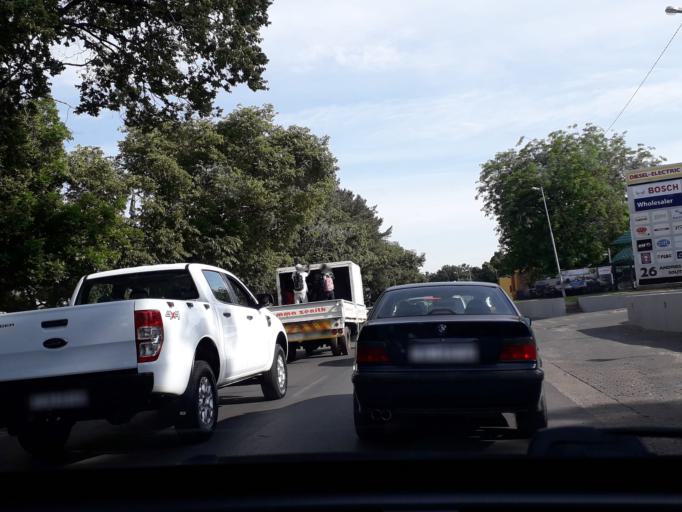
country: ZA
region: Gauteng
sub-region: City of Johannesburg Metropolitan Municipality
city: Modderfontein
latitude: -26.1128
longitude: 28.0784
